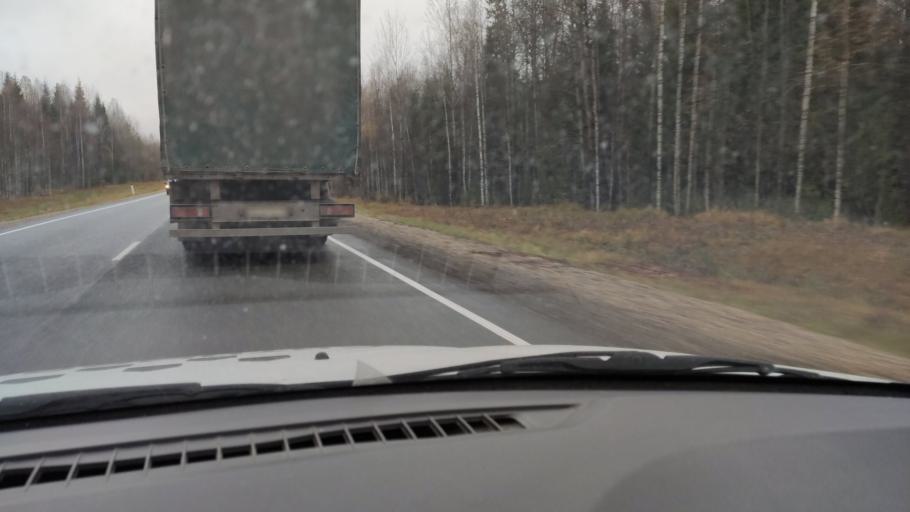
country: RU
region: Kirov
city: Chernaya Kholunitsa
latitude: 58.8006
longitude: 51.8620
